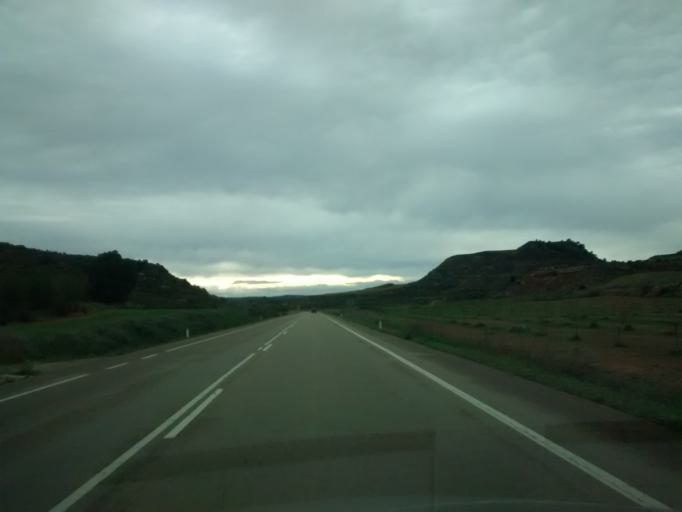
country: ES
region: Aragon
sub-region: Provincia de Zaragoza
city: Caspe
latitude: 41.2086
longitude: 0.0307
